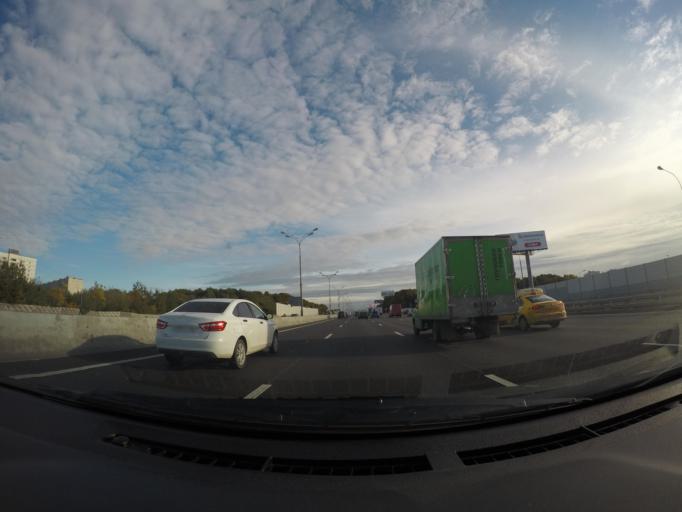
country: RU
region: Moskovskaya
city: Mosrentgen
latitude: 55.6274
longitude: 37.4729
